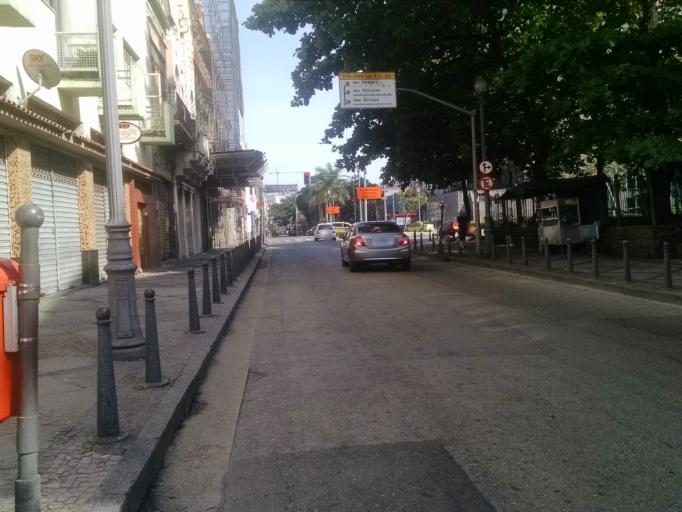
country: BR
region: Rio de Janeiro
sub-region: Rio De Janeiro
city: Rio de Janeiro
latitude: -22.9105
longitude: -43.1827
